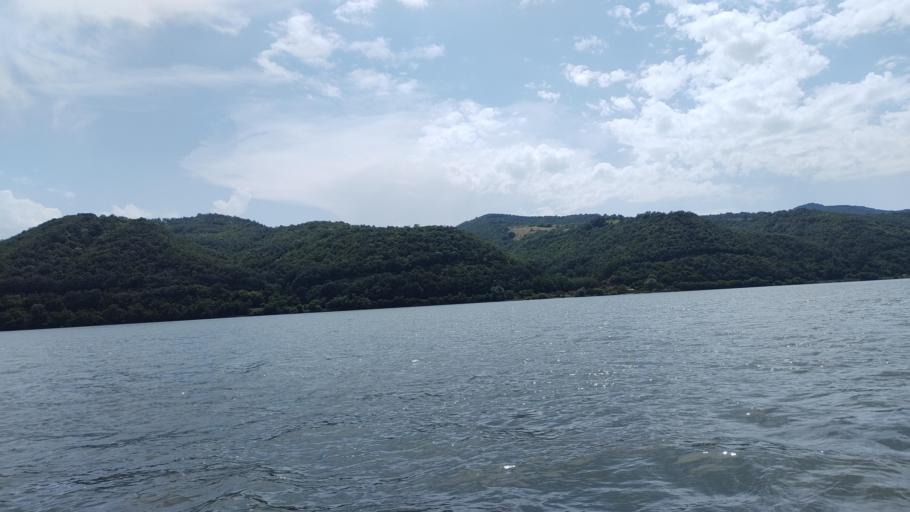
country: RO
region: Caras-Severin
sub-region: Comuna Berzasca
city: Berzasca
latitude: 44.6431
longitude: 21.9364
